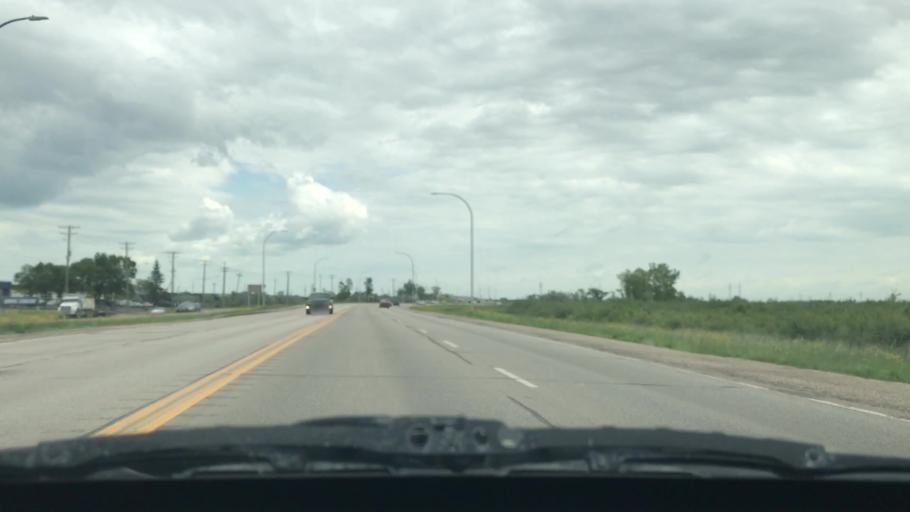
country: CA
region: Manitoba
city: Winnipeg
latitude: 49.8560
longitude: -97.0364
